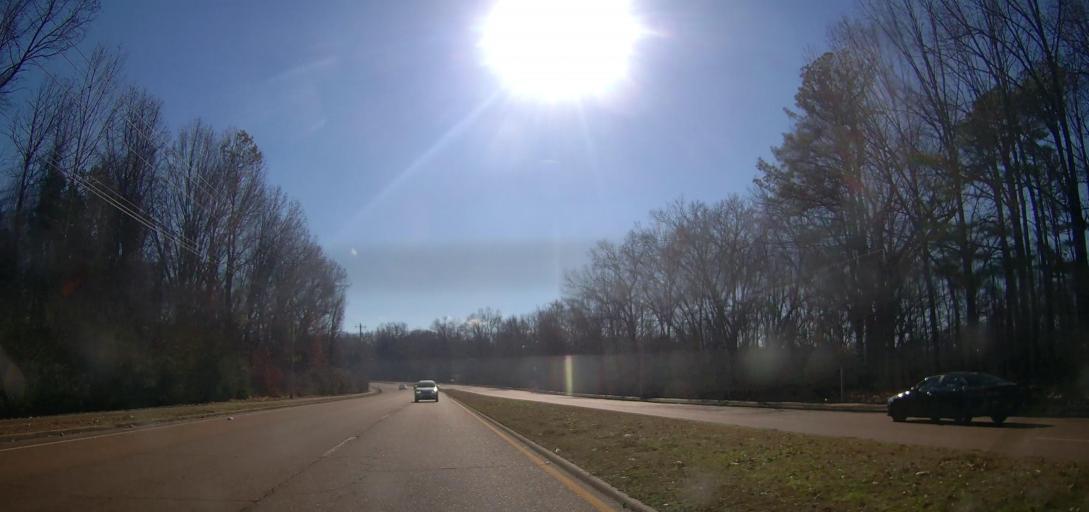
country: US
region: Tennessee
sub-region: Shelby County
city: Bartlett
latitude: 35.2395
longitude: -89.8973
